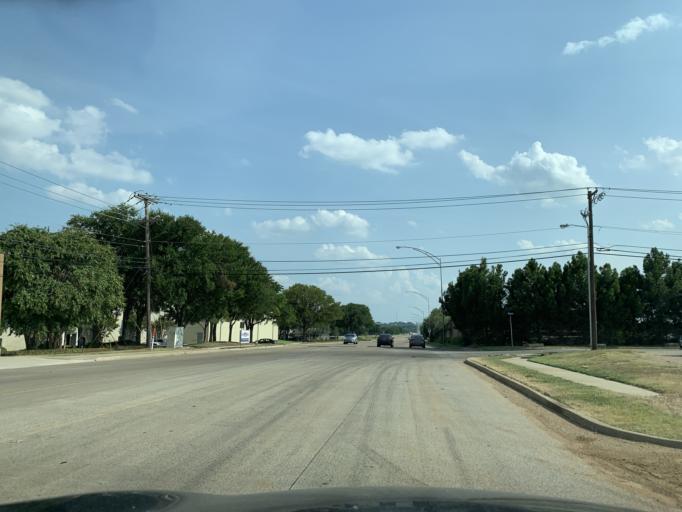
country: US
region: Texas
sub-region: Tarrant County
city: Richland Hills
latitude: 32.7950
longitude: -97.2213
